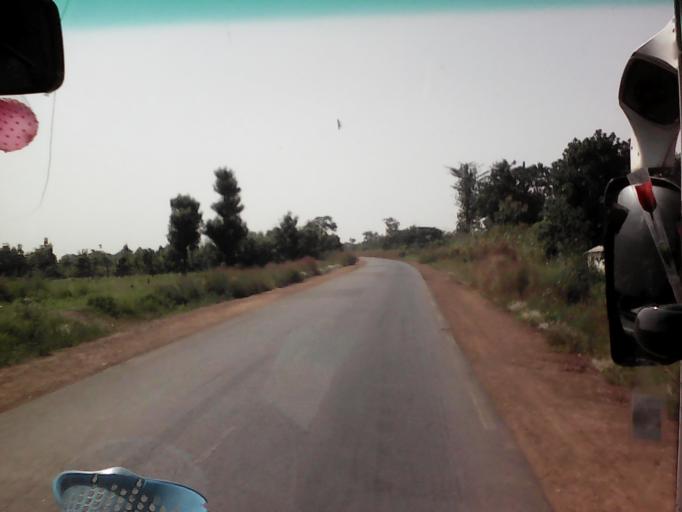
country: TG
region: Centrale
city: Sotouboua
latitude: 8.6915
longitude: 1.0231
